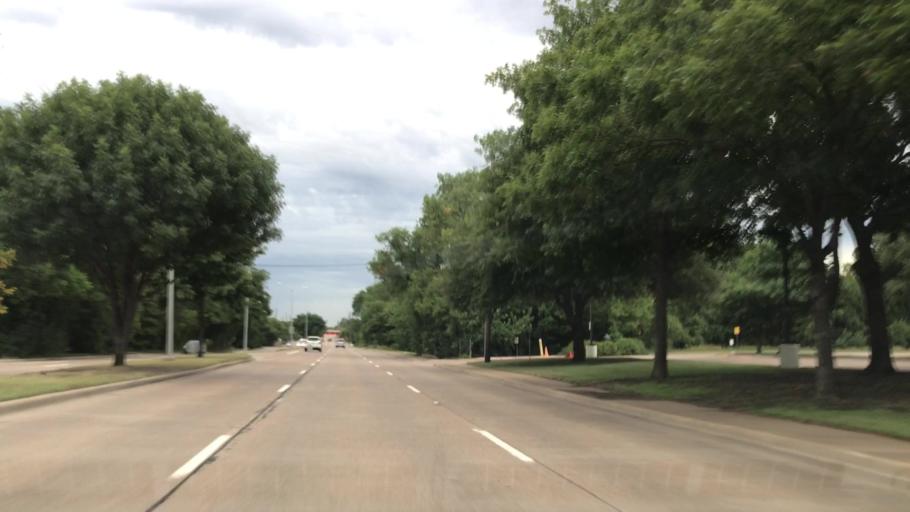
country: US
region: Texas
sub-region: Dallas County
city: Addison
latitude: 32.9318
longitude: -96.7863
